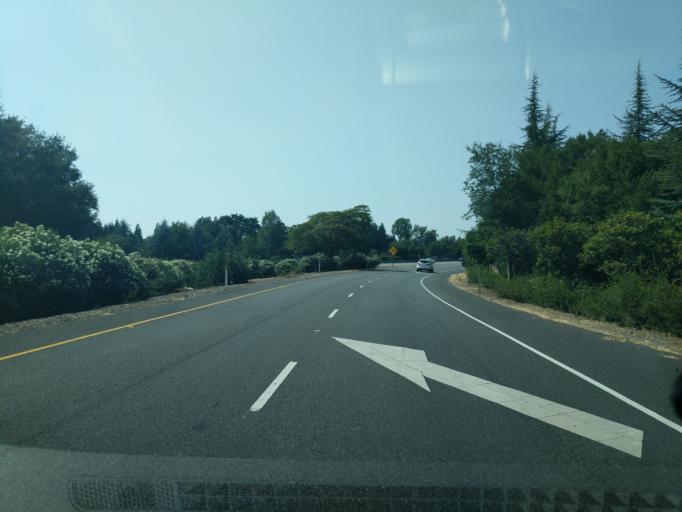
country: US
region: California
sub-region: Contra Costa County
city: San Ramon
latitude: 37.7614
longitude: -121.9653
